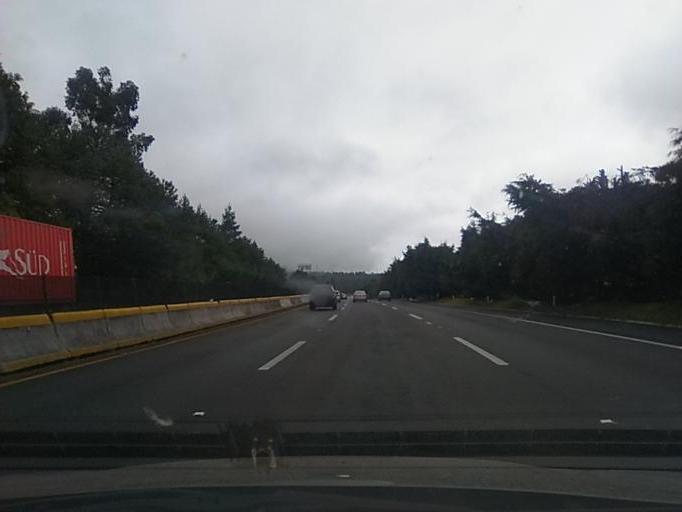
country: MX
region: Morelos
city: Tres Marias
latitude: 19.1198
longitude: -99.1810
